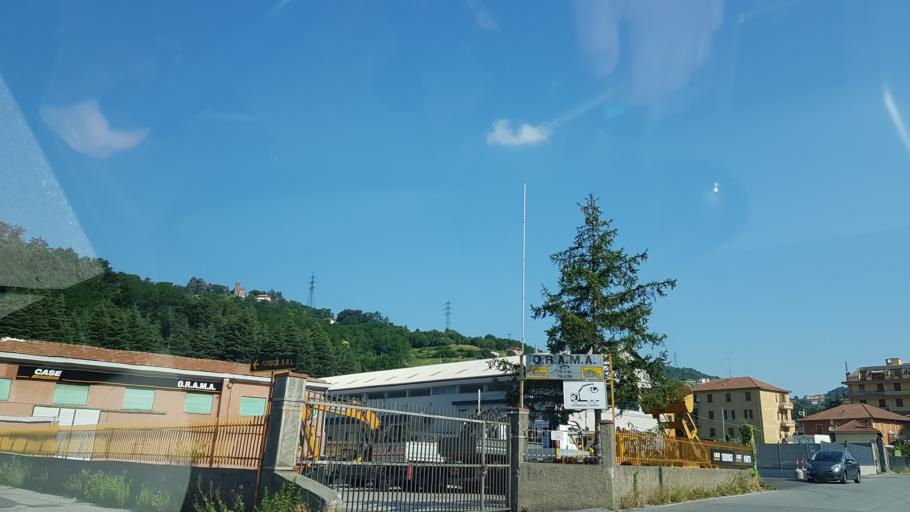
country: IT
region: Liguria
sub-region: Provincia di Genova
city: Manesseno
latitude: 44.4885
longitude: 8.9216
